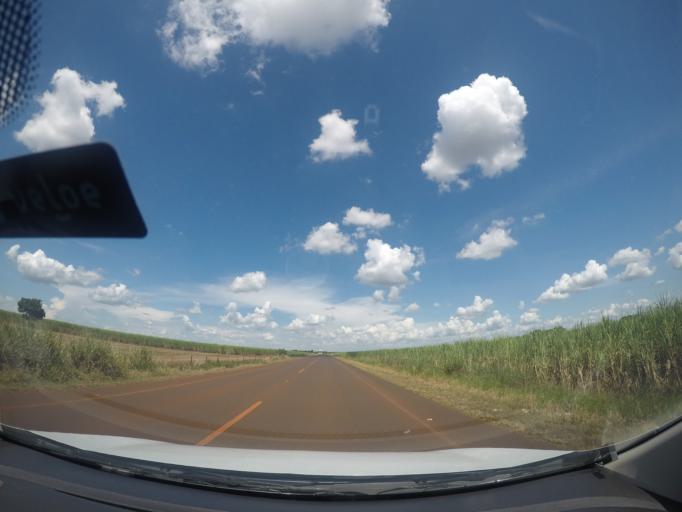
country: BR
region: Minas Gerais
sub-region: Conceicao Das Alagoas
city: Conceicao das Alagoas
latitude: -19.9255
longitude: -48.6686
